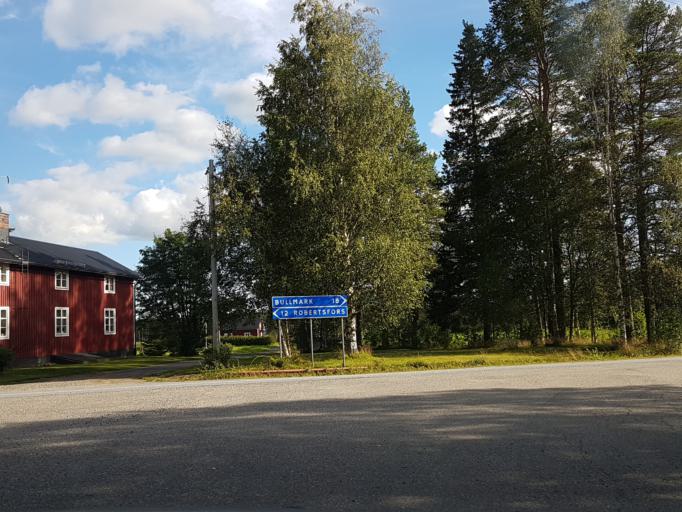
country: SE
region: Vaesterbotten
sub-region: Robertsfors Kommun
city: Robertsfors
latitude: 64.1597
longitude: 20.6529
